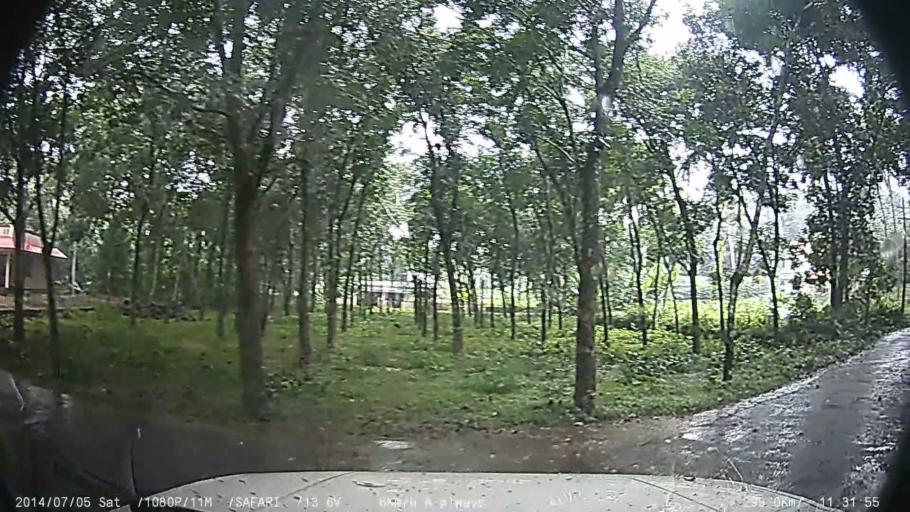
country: IN
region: Kerala
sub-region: Ernakulam
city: Muvattupula
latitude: 9.9703
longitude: 76.6008
